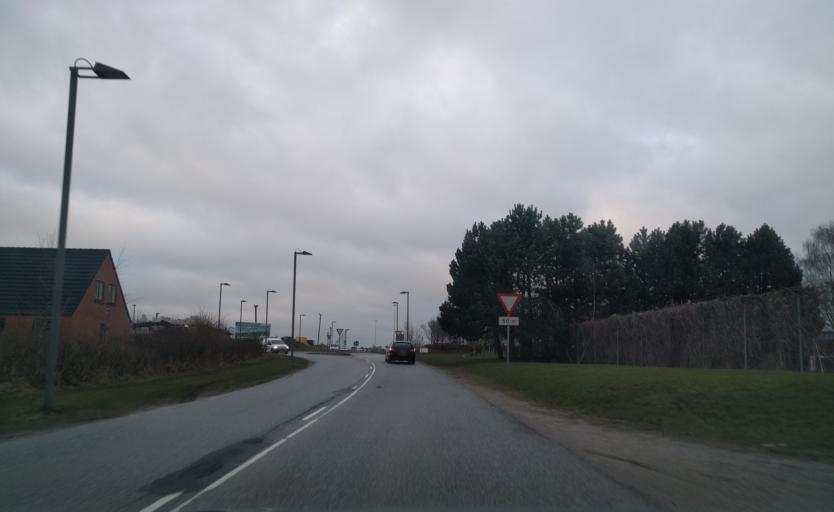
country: DK
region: North Denmark
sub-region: Alborg Kommune
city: Gistrup
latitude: 57.0125
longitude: 9.9794
